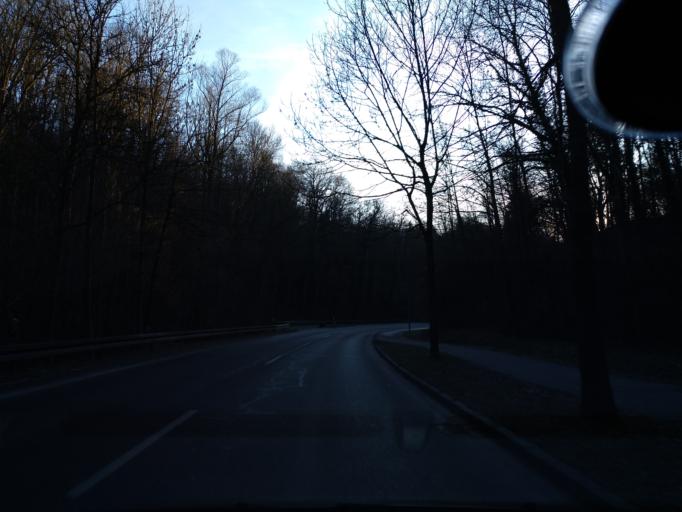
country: DE
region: Baden-Wuerttemberg
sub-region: Regierungsbezirk Stuttgart
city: Schwaebisch Hall
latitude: 49.0986
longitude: 9.7586
